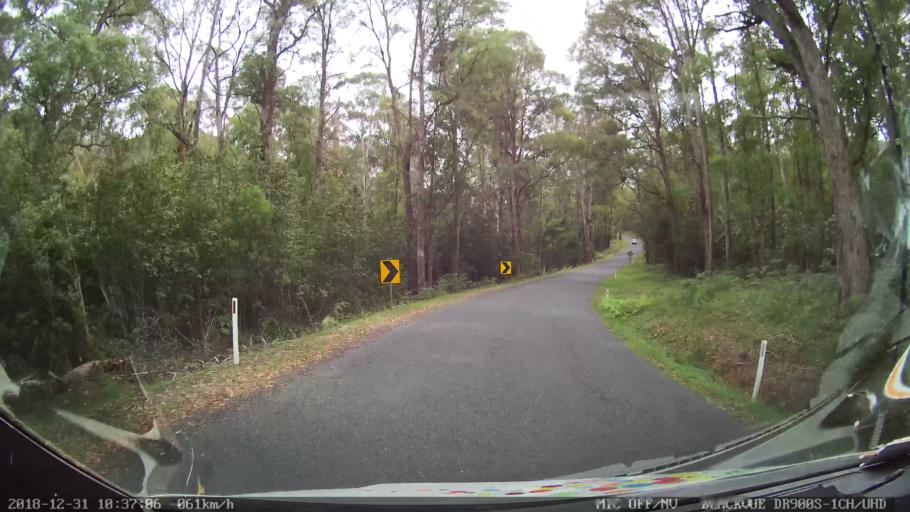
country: AU
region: New South Wales
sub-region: Snowy River
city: Jindabyne
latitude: -36.4193
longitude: 148.1692
